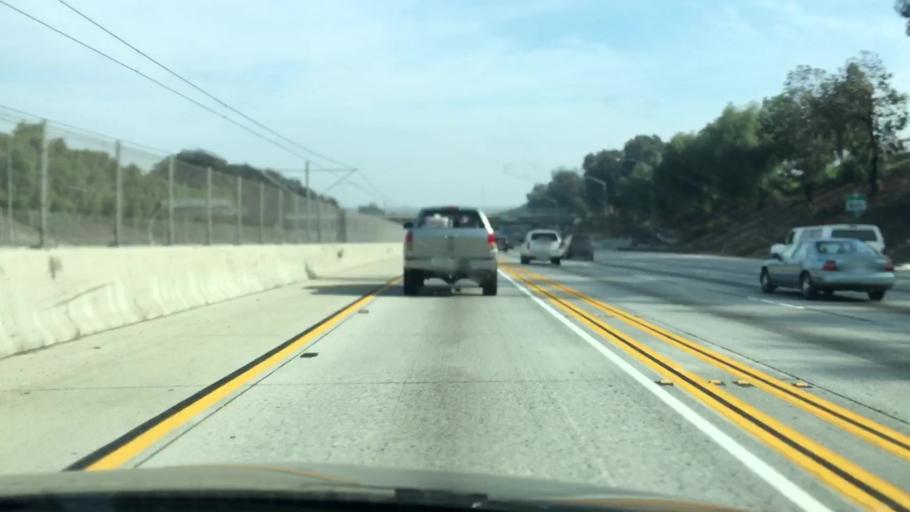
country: US
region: California
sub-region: Los Angeles County
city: Downey
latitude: 33.9130
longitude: -118.1371
